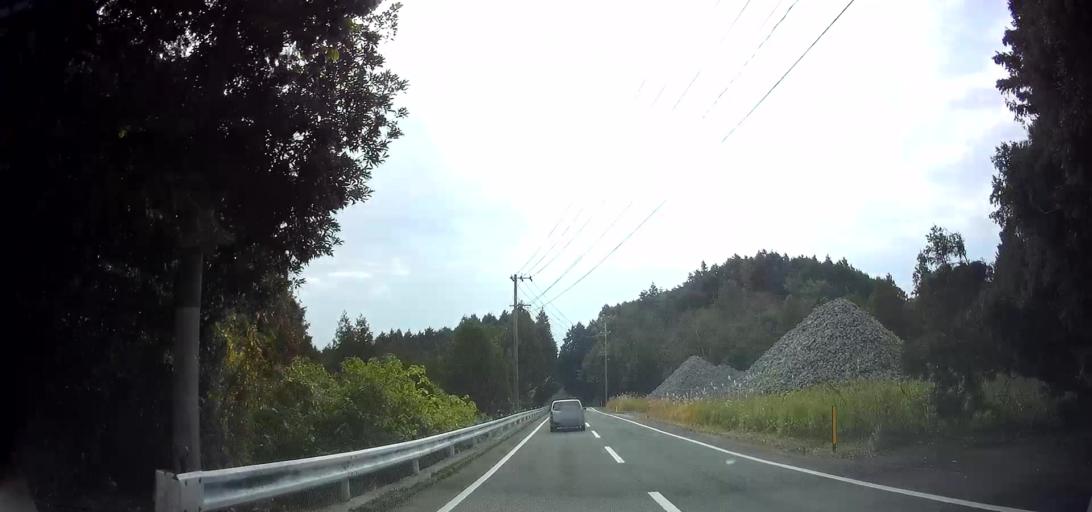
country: JP
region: Nagasaki
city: Shimabara
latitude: 32.6945
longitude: 130.2547
